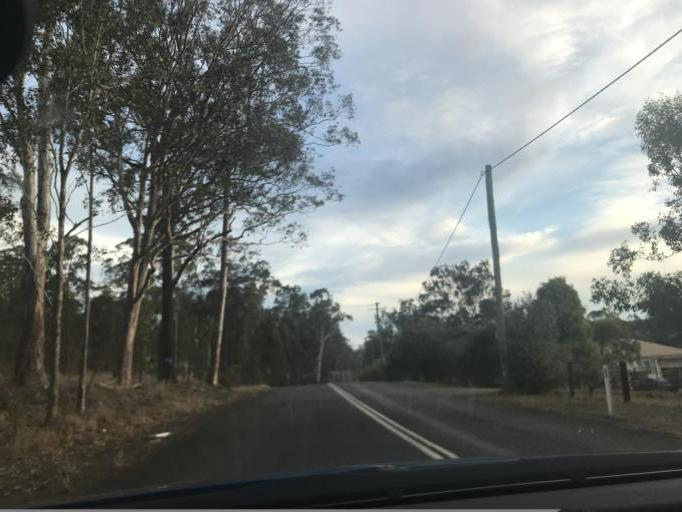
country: AU
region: New South Wales
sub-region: Cessnock
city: Cessnock
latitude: -32.8988
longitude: 151.2934
